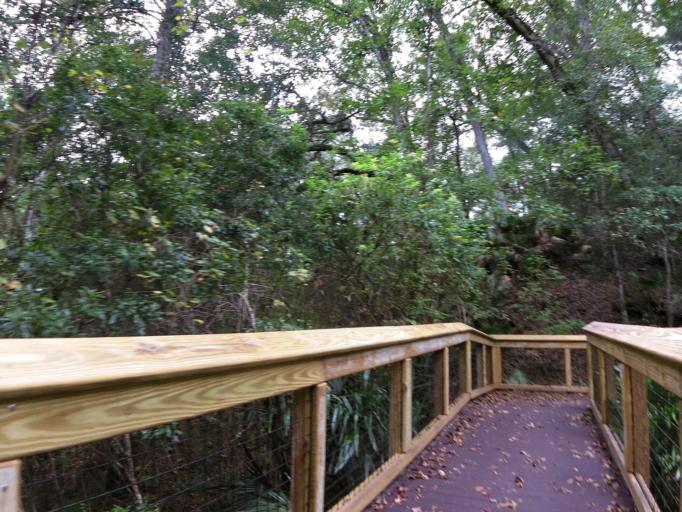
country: US
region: Florida
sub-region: Clay County
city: Keystone Heights
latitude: 29.8390
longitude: -81.9517
